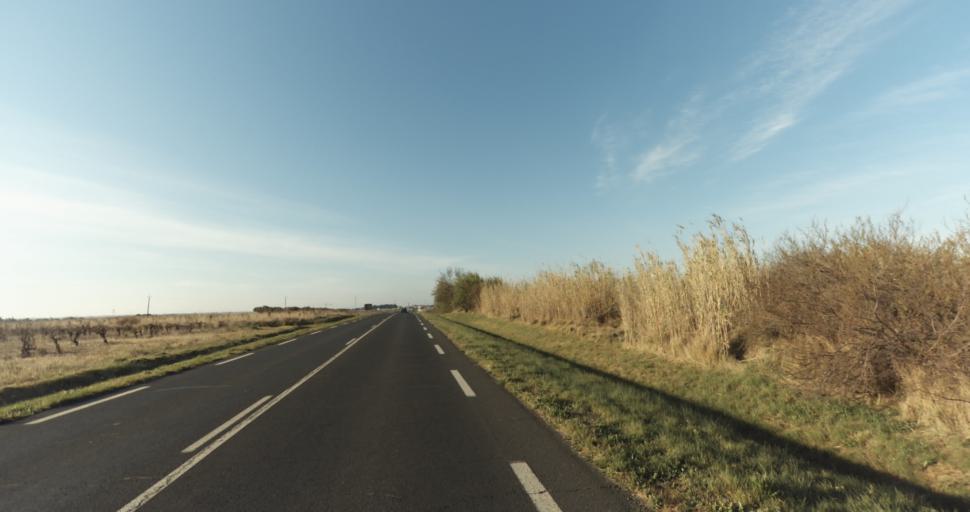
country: FR
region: Languedoc-Roussillon
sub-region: Departement de l'Herault
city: Marseillan
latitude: 43.3755
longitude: 3.5339
